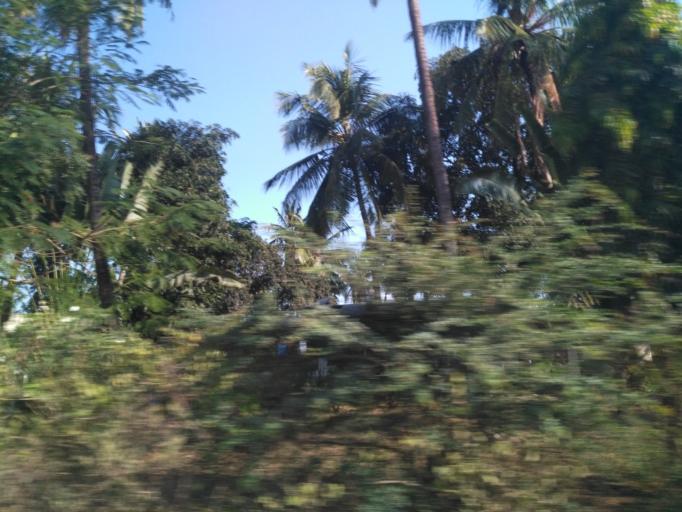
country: TZ
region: Dar es Salaam
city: Dar es Salaam
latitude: -6.8495
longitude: 39.3169
